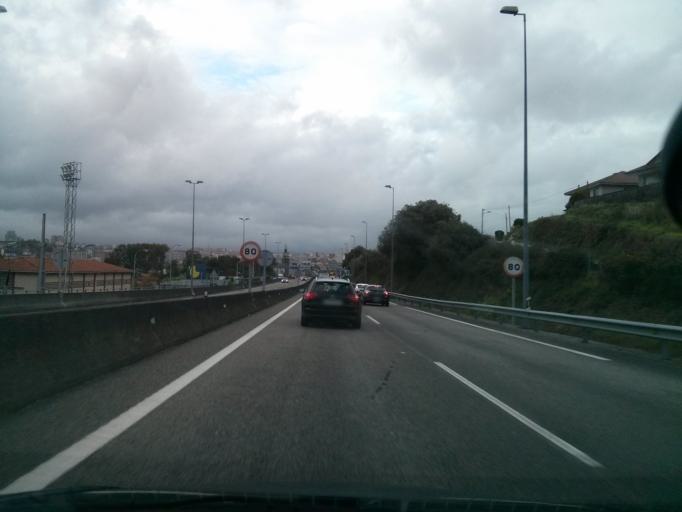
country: ES
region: Galicia
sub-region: Provincia de Pontevedra
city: Vigo
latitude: 42.2106
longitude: -8.6982
